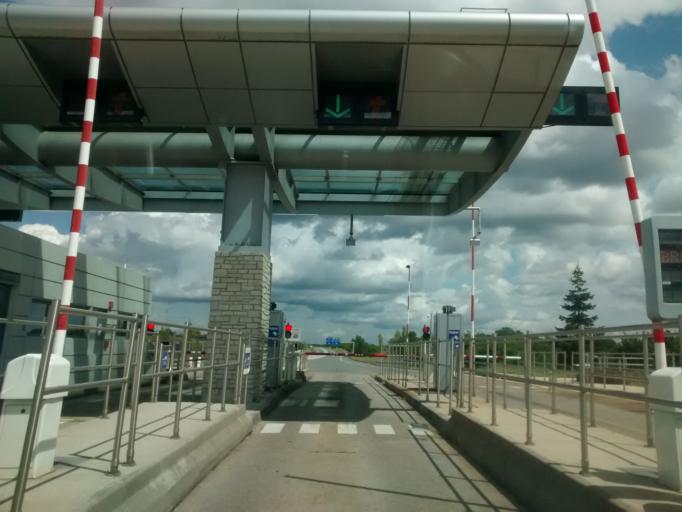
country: FR
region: Midi-Pyrenees
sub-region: Departement du Lot
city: Lalbenque
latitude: 44.3426
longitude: 1.4938
